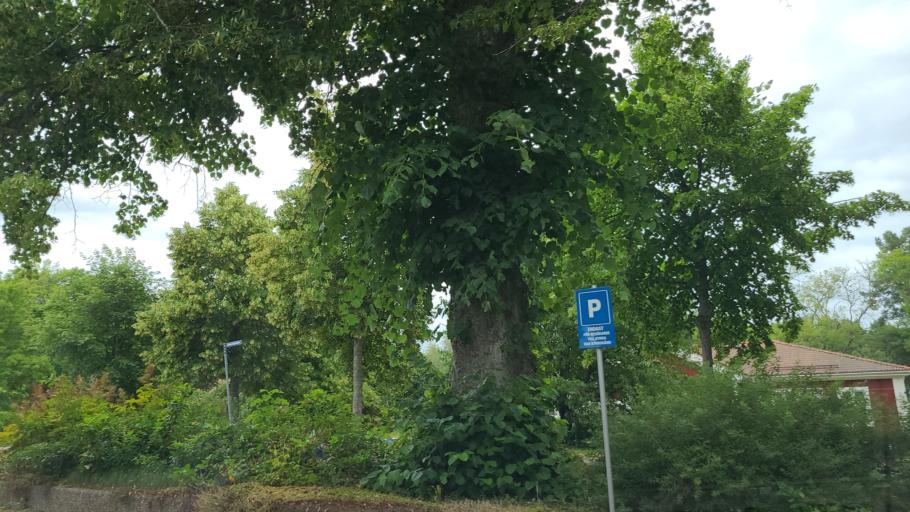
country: SE
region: Stockholm
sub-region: Upplands-Bro Kommun
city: Bro
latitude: 59.5092
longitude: 17.5665
